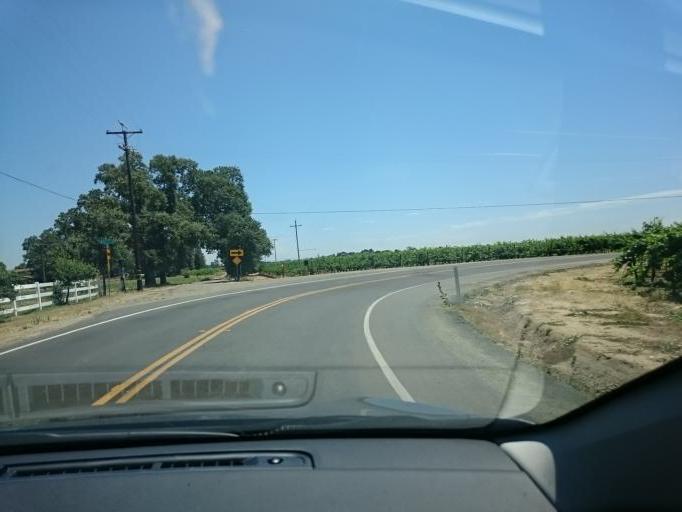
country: US
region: California
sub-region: San Joaquin County
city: Thornton
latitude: 38.2038
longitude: -121.3730
